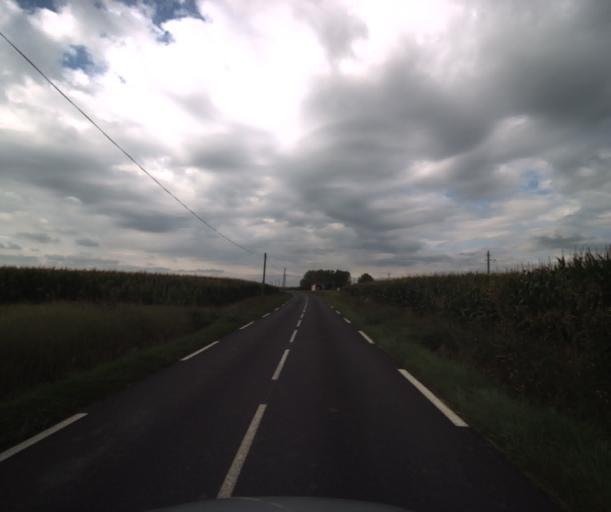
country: FR
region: Midi-Pyrenees
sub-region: Departement de la Haute-Garonne
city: Lacasse
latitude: 43.4132
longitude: 1.2719
